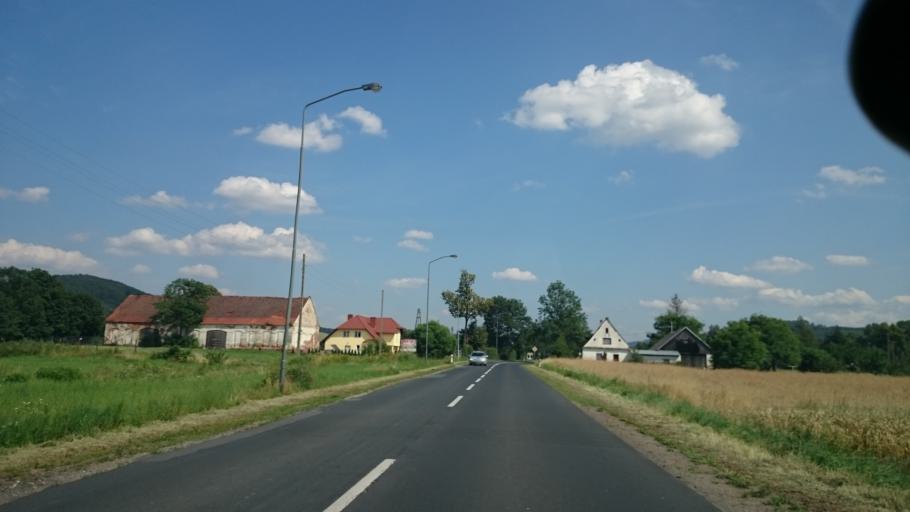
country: PL
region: Lower Silesian Voivodeship
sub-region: Powiat klodzki
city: Klodzko
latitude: 50.3682
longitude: 16.6838
